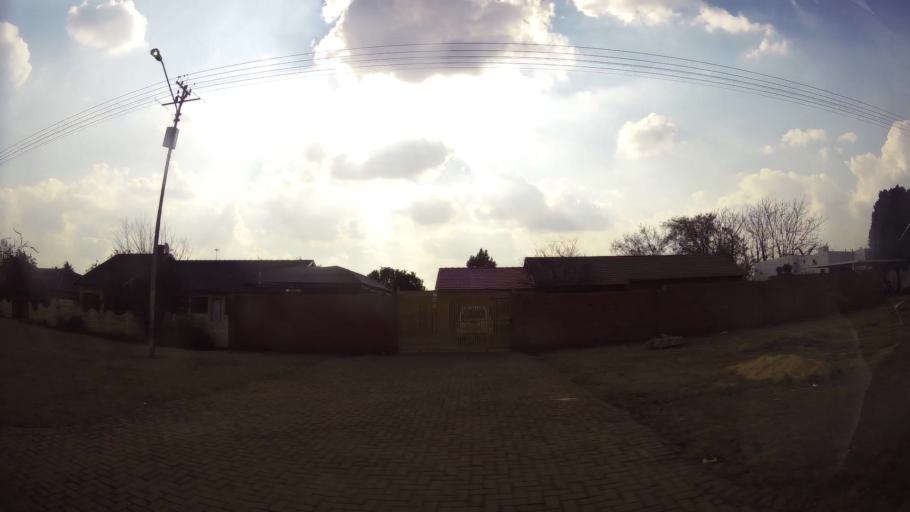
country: ZA
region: Gauteng
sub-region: Ekurhuleni Metropolitan Municipality
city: Germiston
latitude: -26.3029
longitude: 28.1833
